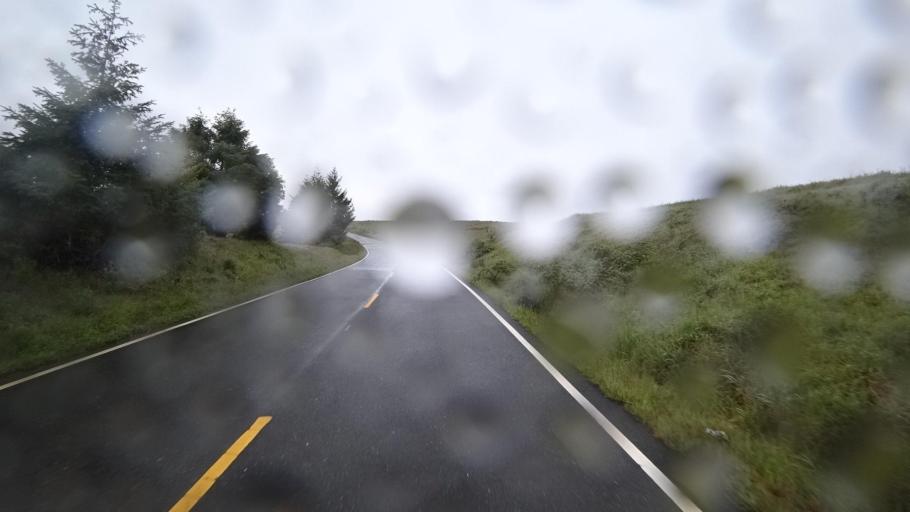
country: US
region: California
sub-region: Humboldt County
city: Westhaven-Moonstone
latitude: 41.1723
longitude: -123.9201
